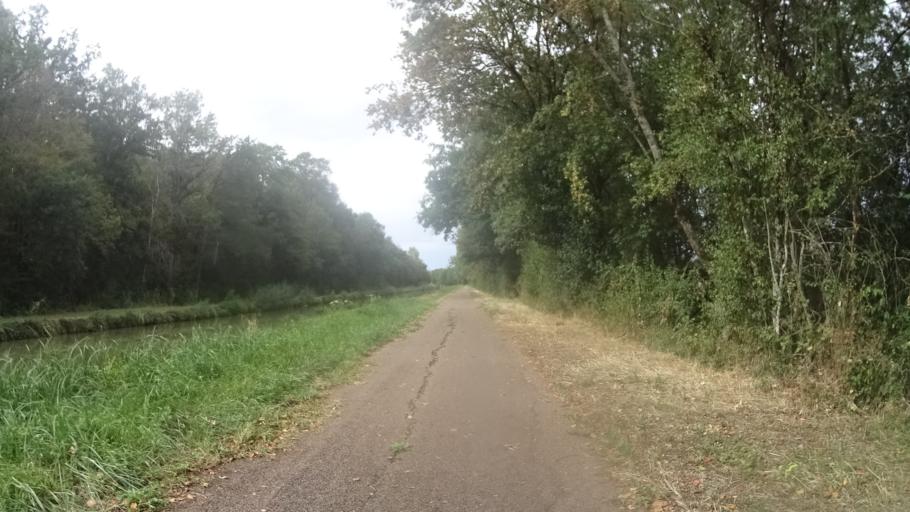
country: FR
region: Bourgogne
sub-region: Departement de la Nievre
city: Sermoise-sur-Loire
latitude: 46.9532
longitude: 3.2000
